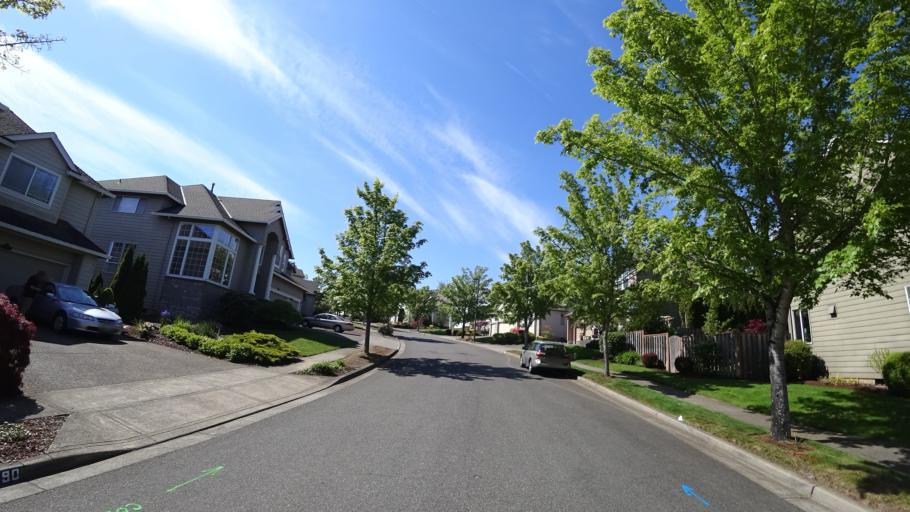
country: US
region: Oregon
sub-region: Washington County
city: King City
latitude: 45.4323
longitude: -122.8411
